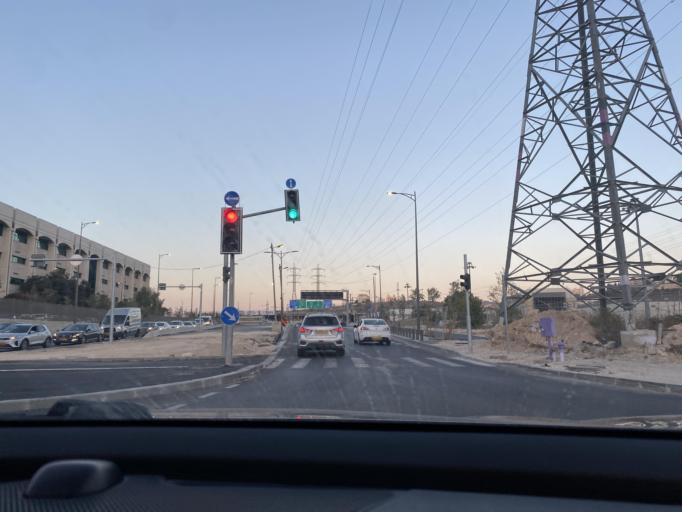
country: PS
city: Khallat Hamamah
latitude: 31.7486
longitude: 35.1857
